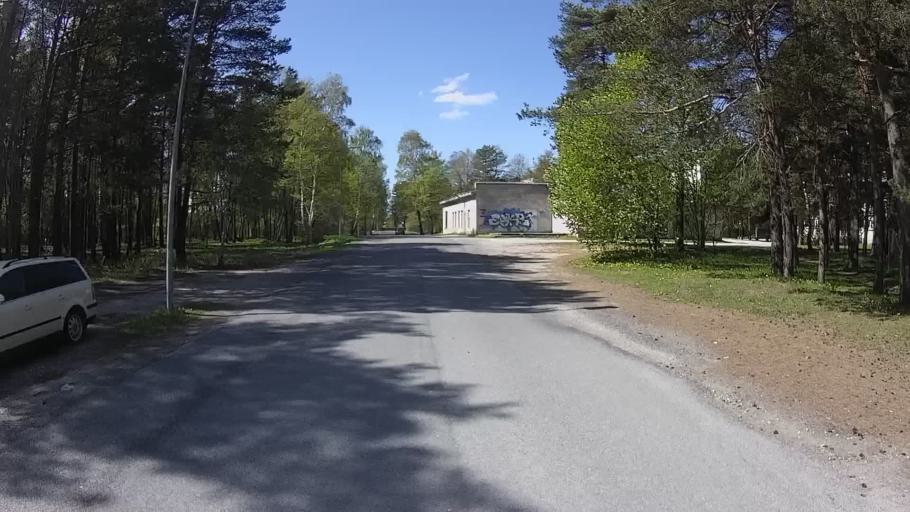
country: EE
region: Laeaene
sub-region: Haapsalu linn
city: Haapsalu
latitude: 58.9338
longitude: 23.5528
